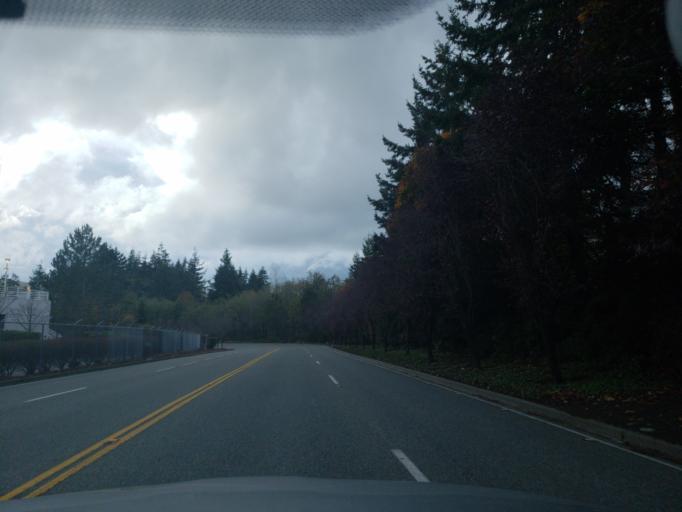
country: US
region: Washington
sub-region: Snohomish County
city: Mukilteo
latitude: 47.9327
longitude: -122.2636
